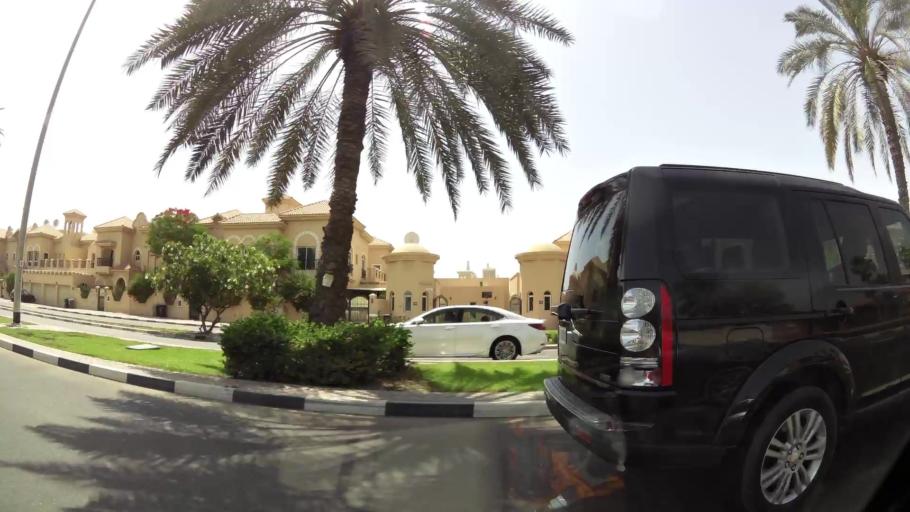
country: AE
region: Dubai
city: Dubai
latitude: 25.1355
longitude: 55.2008
